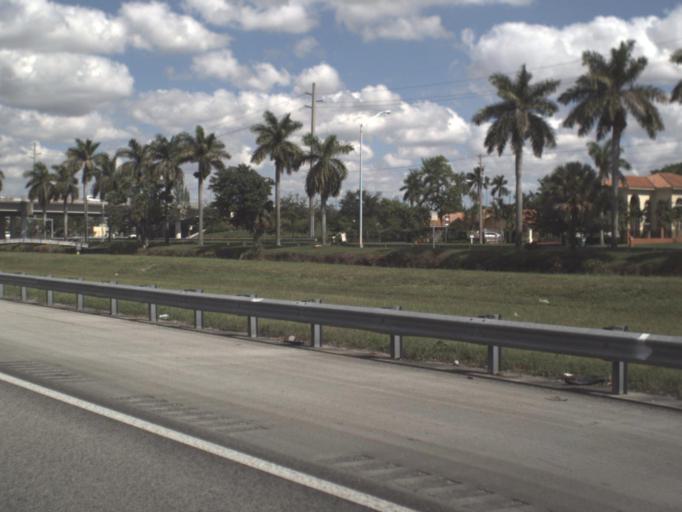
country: US
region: Florida
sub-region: Miami-Dade County
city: University Park
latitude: 25.7447
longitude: -80.3846
